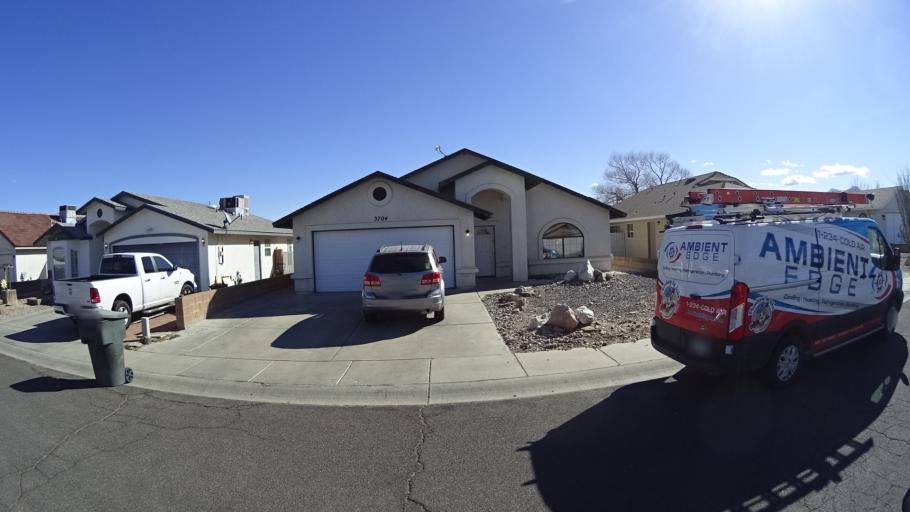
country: US
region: Arizona
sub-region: Mohave County
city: New Kingman-Butler
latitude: 35.2307
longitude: -114.0225
